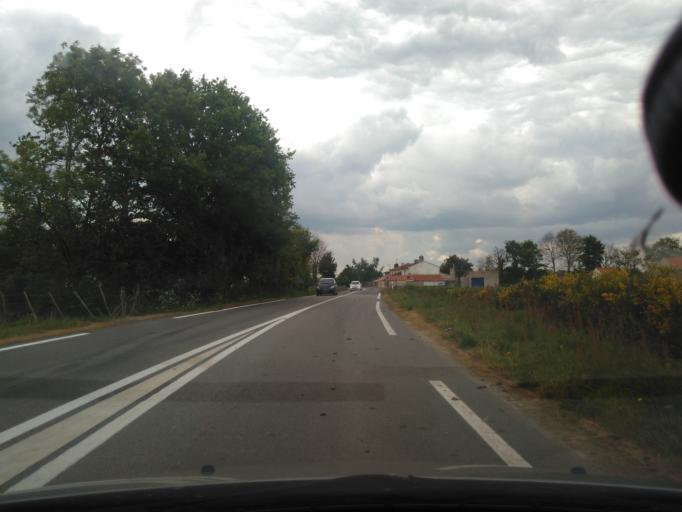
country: FR
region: Pays de la Loire
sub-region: Departement de la Vendee
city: Mouilleron-le-Captif
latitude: 46.7094
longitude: -1.4146
